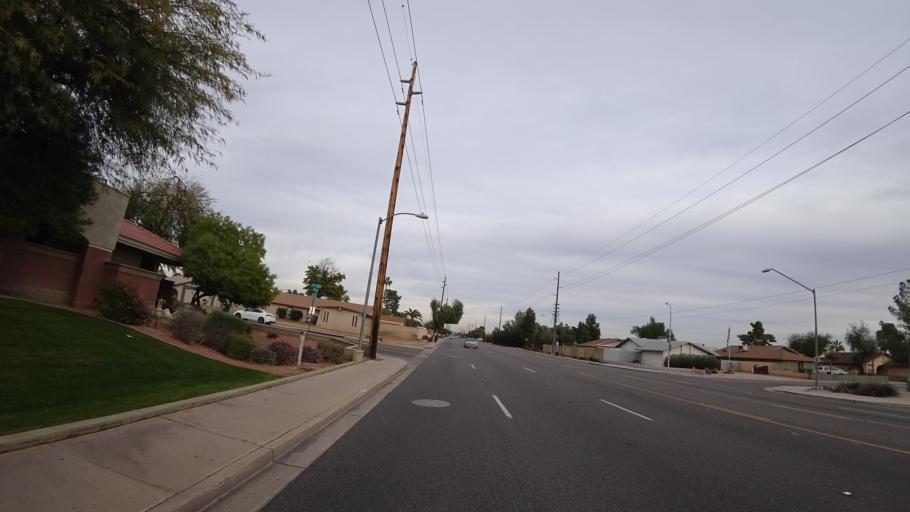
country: US
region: Arizona
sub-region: Maricopa County
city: Glendale
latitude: 33.5676
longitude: -112.1822
